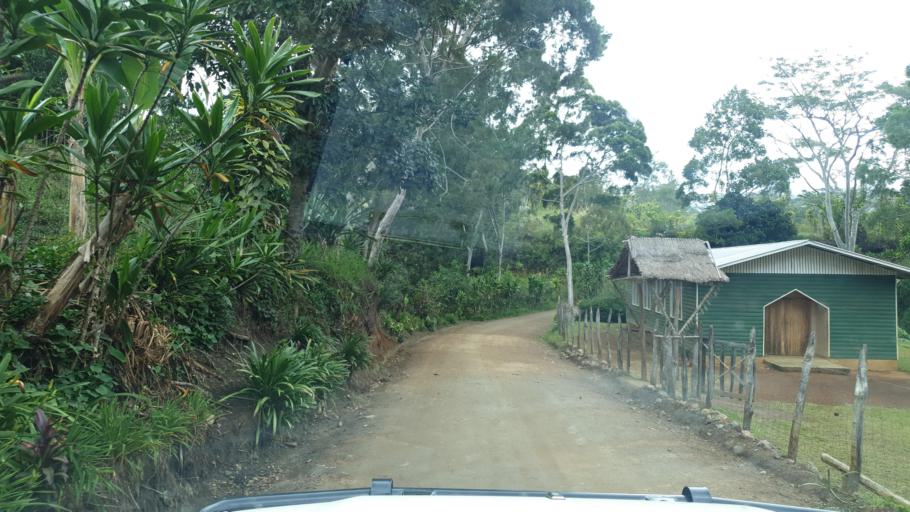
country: PG
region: Eastern Highlands
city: Goroka
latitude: -5.9490
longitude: 145.2709
